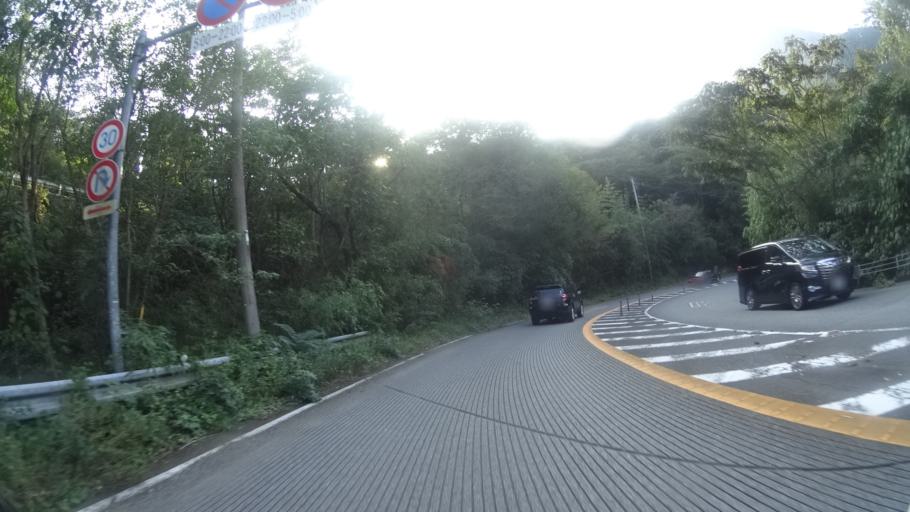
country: JP
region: Oita
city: Beppu
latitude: 33.2766
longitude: 131.4499
